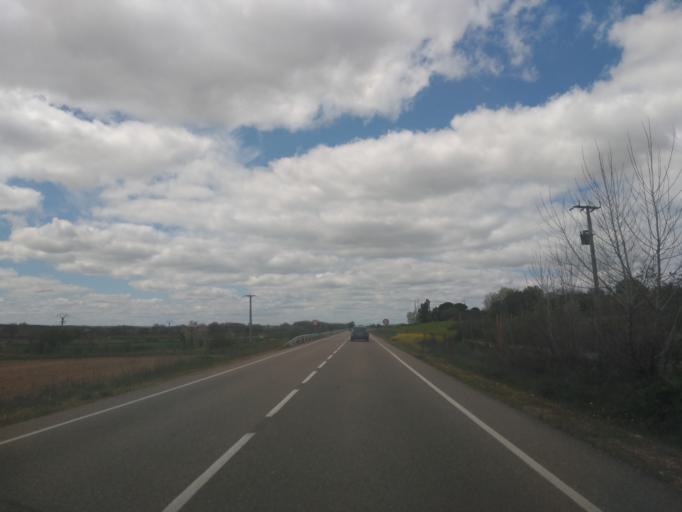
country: ES
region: Castille and Leon
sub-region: Provincia de Salamanca
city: Valverdon
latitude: 41.0495
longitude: -5.7825
